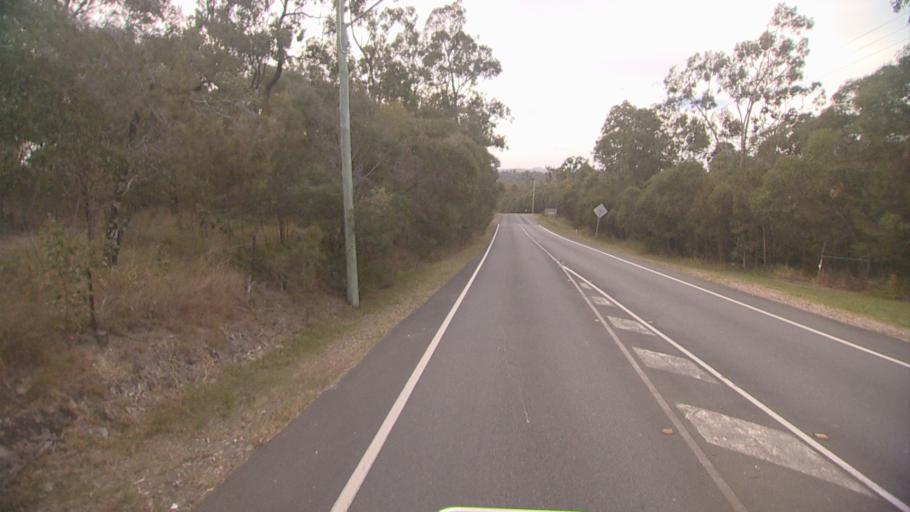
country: AU
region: Queensland
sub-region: Logan
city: Windaroo
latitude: -27.7258
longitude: 153.1733
